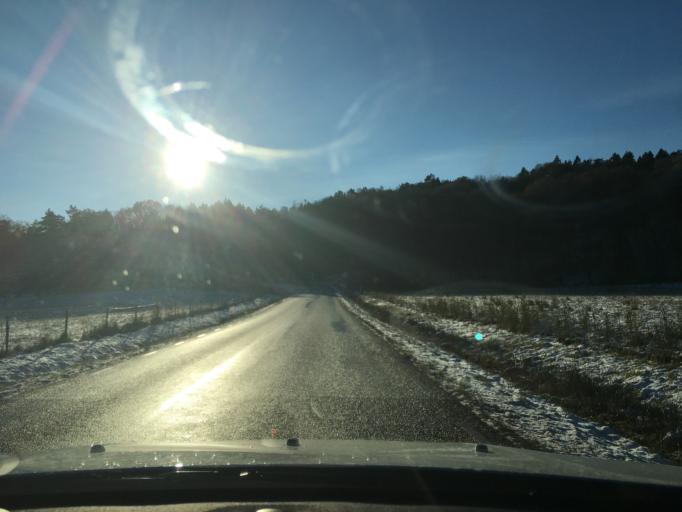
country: SE
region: Vaestra Goetaland
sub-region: Tjorns Kommun
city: Myggenas
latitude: 58.0518
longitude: 11.6740
